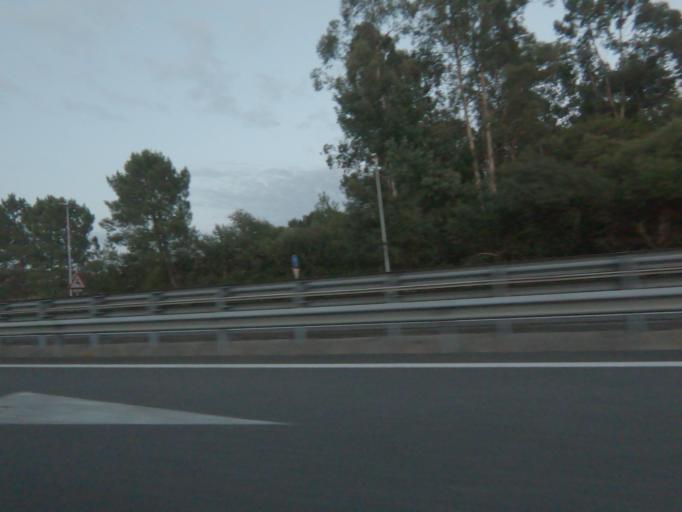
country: ES
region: Galicia
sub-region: Provincia de Pontevedra
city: Tui
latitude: 42.0962
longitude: -8.6255
